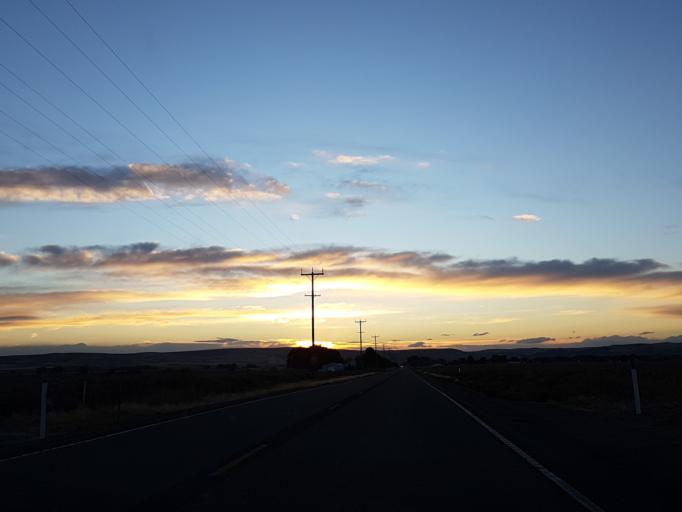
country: US
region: Oregon
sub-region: Malheur County
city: Vale
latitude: 43.9392
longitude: -117.3507
